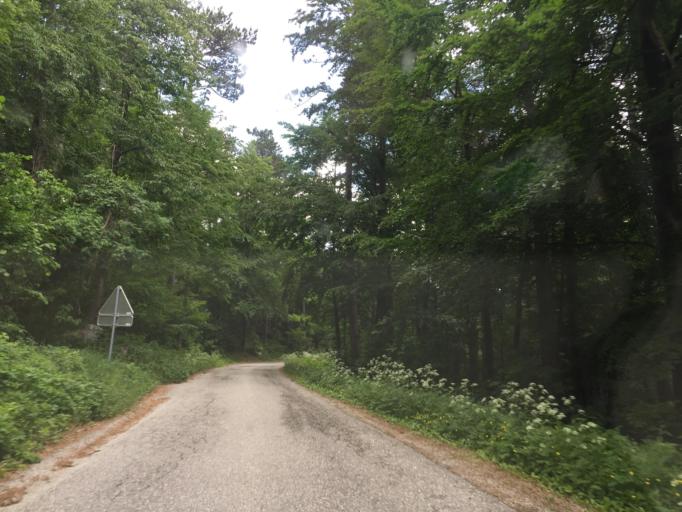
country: SI
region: Nova Gorica
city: Sempas
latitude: 46.0257
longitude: 13.7518
